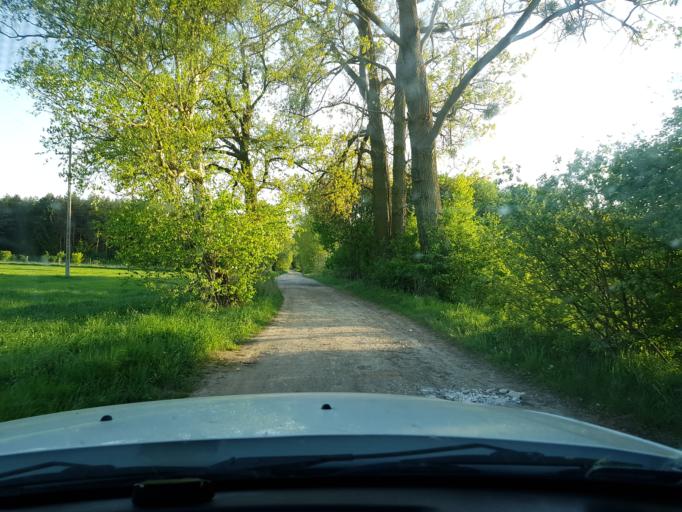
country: PL
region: West Pomeranian Voivodeship
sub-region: Powiat stargardzki
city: Kobylanka
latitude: 53.4135
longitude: 14.9010
